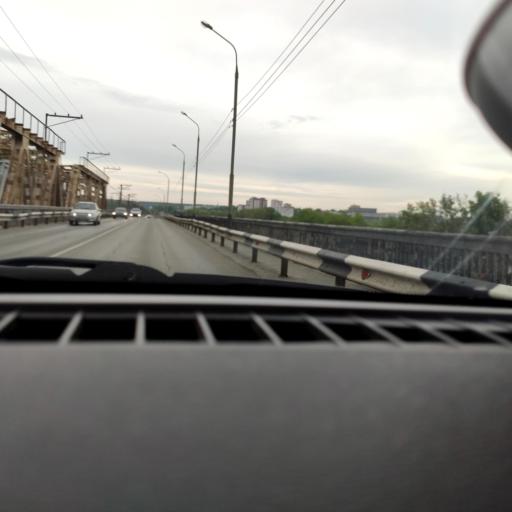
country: RU
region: Perm
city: Perm
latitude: 58.1148
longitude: 56.3452
